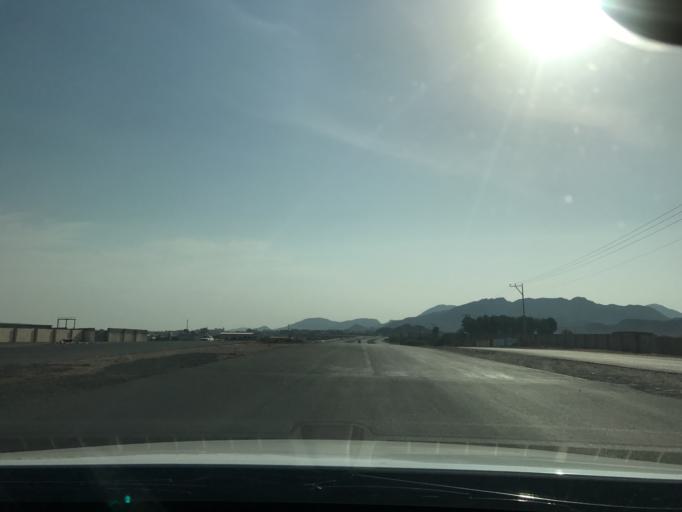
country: SA
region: Makkah
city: Al Jumum
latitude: 21.4537
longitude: 39.5346
